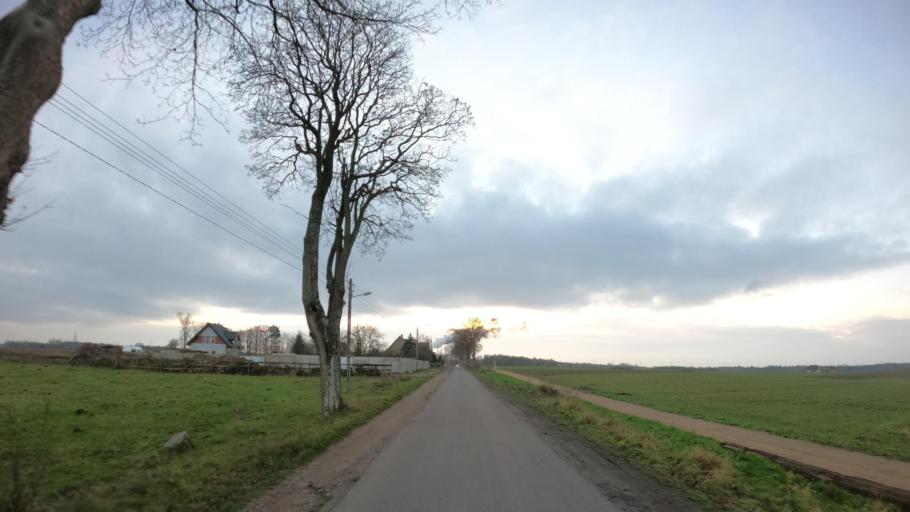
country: PL
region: West Pomeranian Voivodeship
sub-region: Powiat bialogardzki
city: Karlino
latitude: 54.0748
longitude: 15.8823
